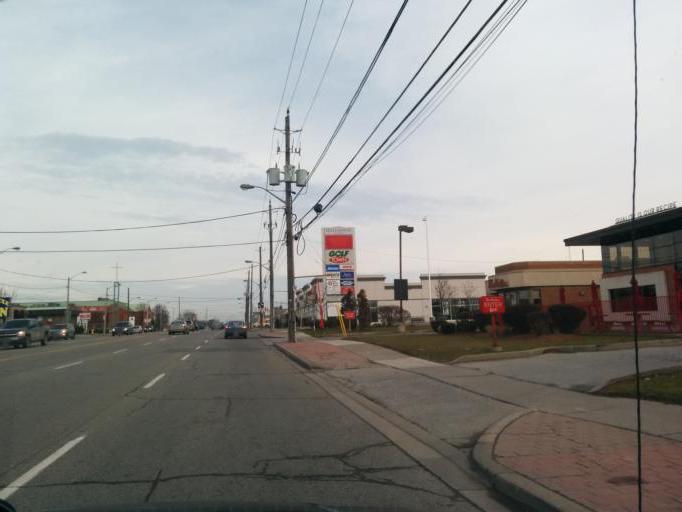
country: CA
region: Ontario
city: Etobicoke
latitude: 43.6178
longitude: -79.5402
